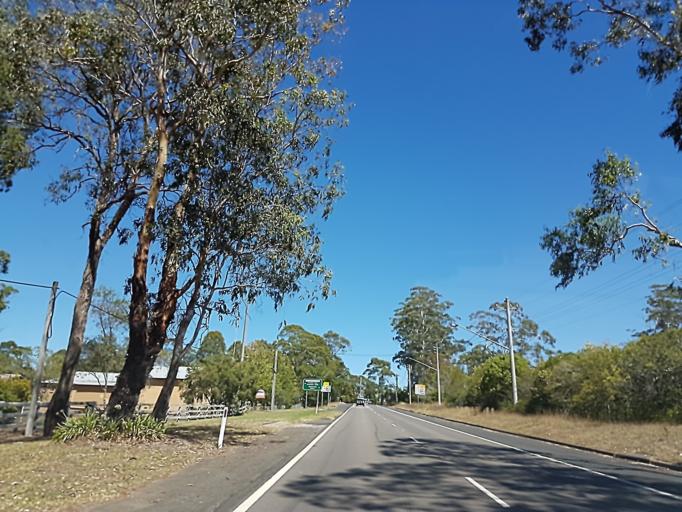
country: AU
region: New South Wales
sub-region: The Hills Shire
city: Kenthurst
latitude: -33.6443
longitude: 151.0249
